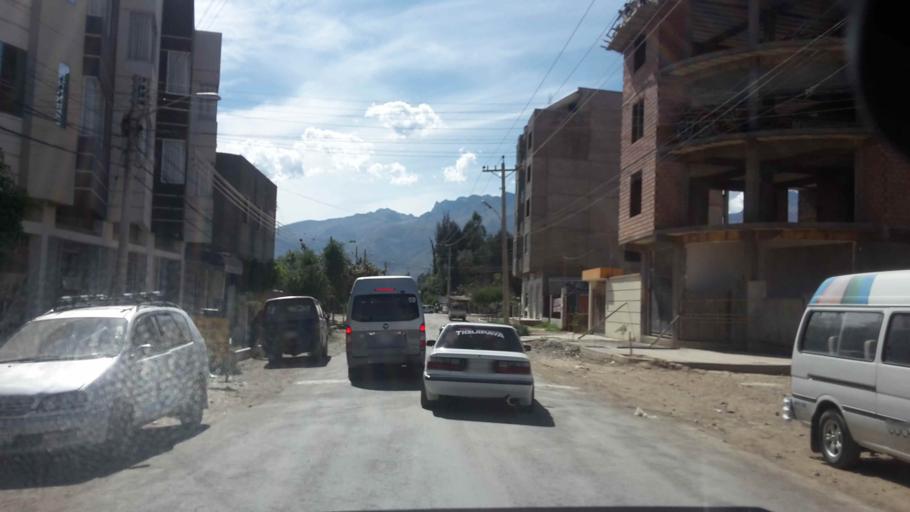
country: BO
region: Cochabamba
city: Cochabamba
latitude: -17.3366
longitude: -66.2227
